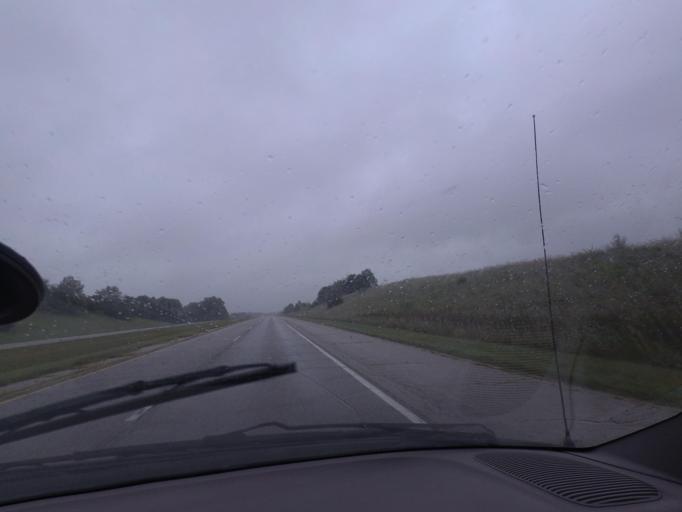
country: US
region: Illinois
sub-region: Pike County
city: Pittsfield
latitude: 39.6881
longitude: -90.8999
